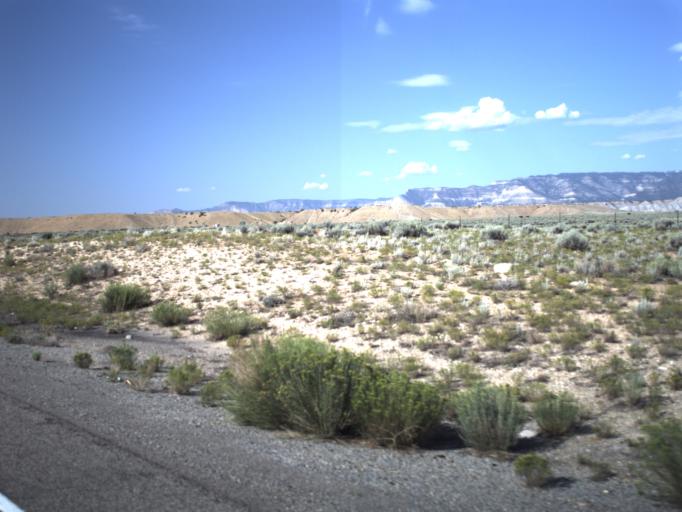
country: US
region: Utah
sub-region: Carbon County
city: Price
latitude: 39.4806
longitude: -110.8526
